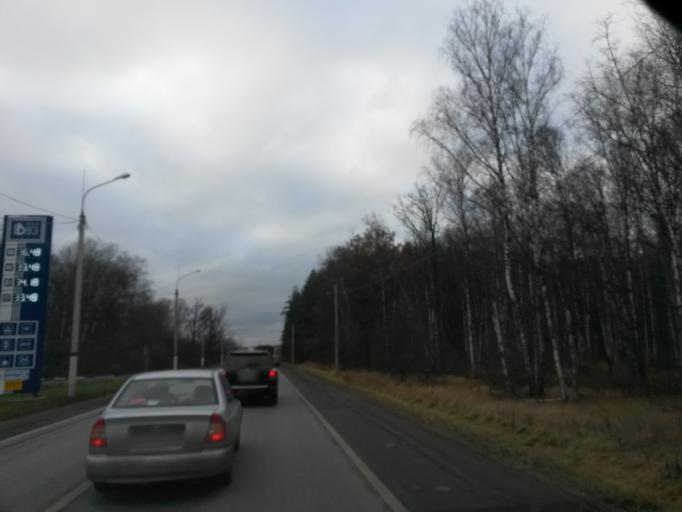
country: RU
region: Moskovskaya
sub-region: Chekhovskiy Rayon
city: Chekhov
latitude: 55.1876
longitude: 37.5116
